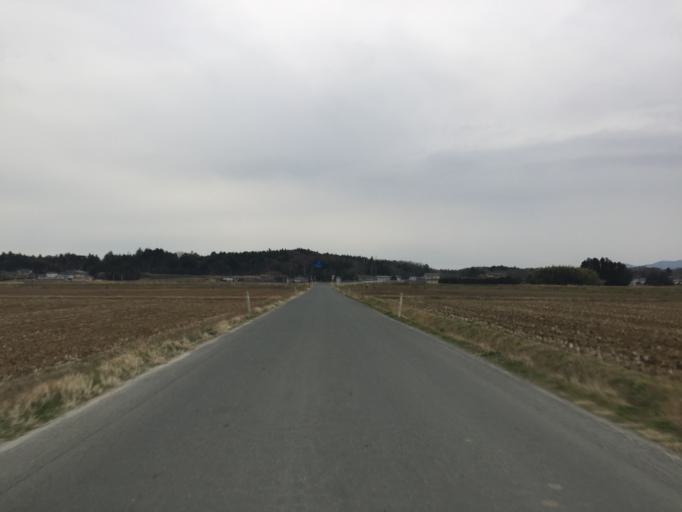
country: JP
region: Miyagi
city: Marumori
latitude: 37.7622
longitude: 140.9387
